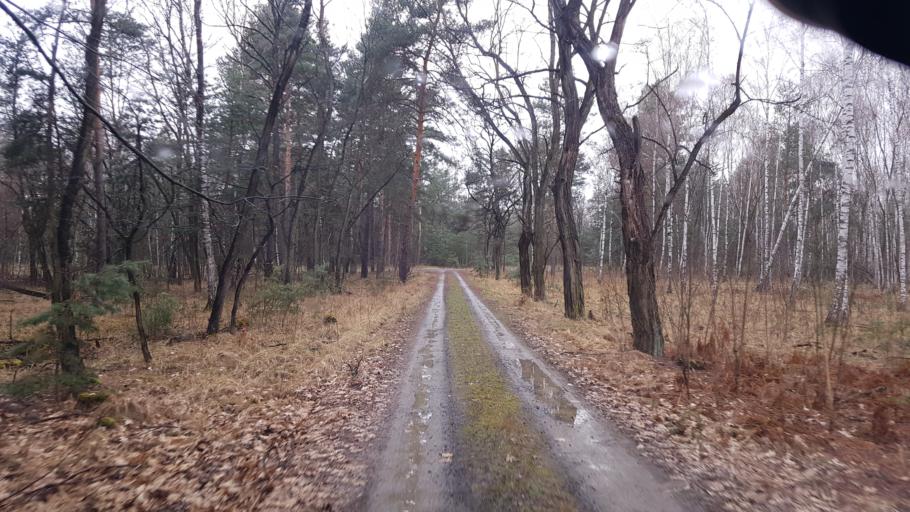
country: DE
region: Brandenburg
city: Grossraschen
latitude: 51.6192
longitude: 13.9693
